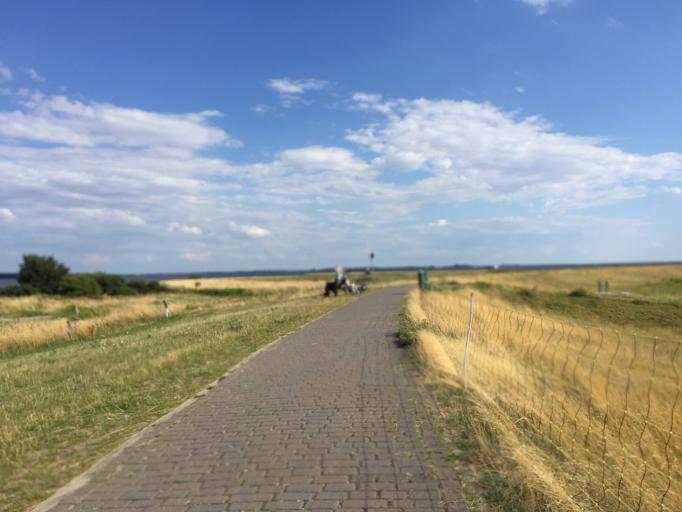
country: DE
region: Mecklenburg-Vorpommern
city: Hiddensee
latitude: 54.5772
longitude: 13.1137
